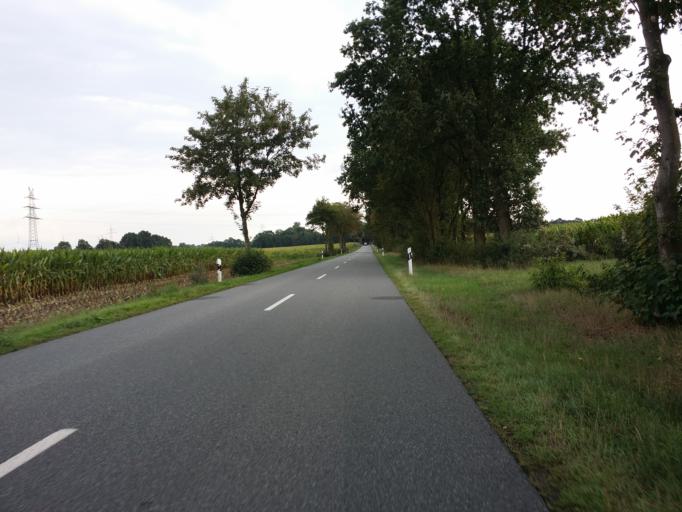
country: DE
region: Lower Saxony
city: Hollnseth
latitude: 53.5803
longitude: 9.1108
